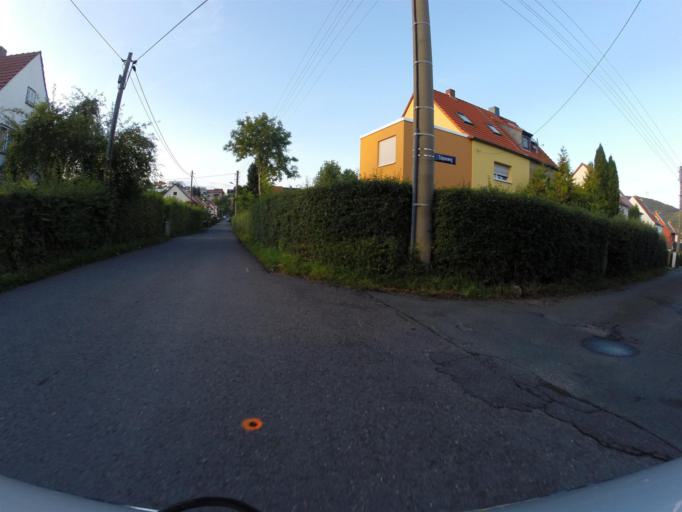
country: DE
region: Thuringia
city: Jena
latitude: 50.9051
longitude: 11.5745
